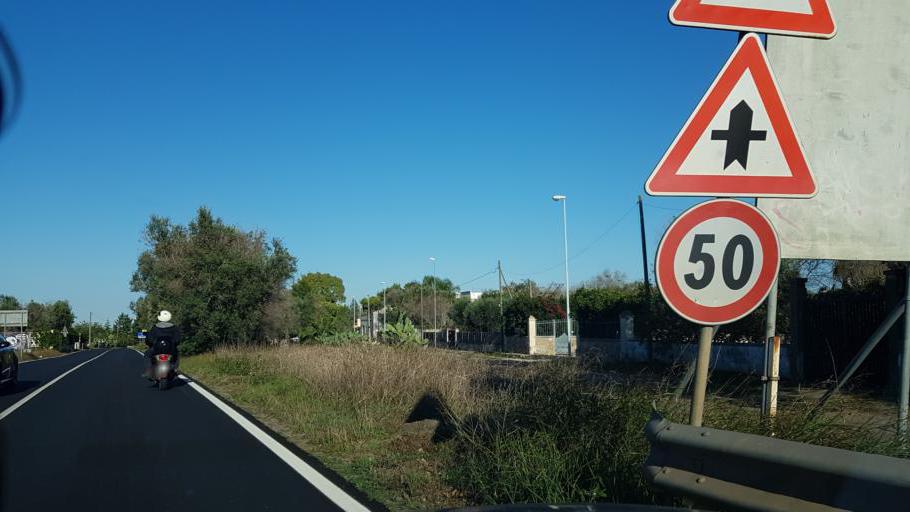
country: IT
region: Apulia
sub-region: Provincia di Lecce
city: Monteroni di Lecce
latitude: 40.3253
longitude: 18.0787
